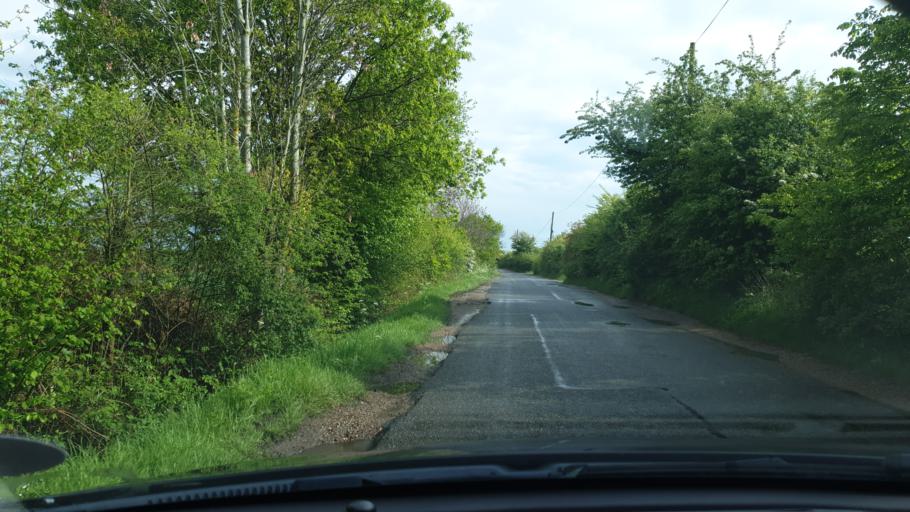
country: GB
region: England
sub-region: Essex
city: Great Bentley
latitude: 51.8406
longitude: 1.0505
